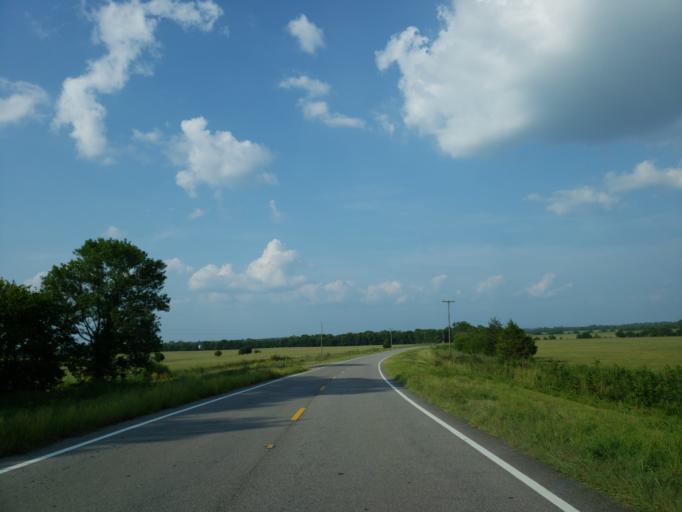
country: US
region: Alabama
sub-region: Greene County
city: Eutaw
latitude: 32.7901
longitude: -87.9741
